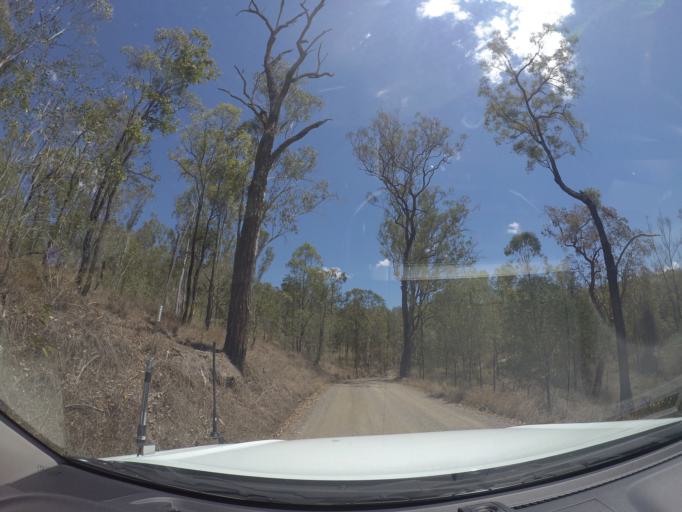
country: AU
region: Queensland
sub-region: Ipswich
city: Springfield Lakes
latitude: -27.8081
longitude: 152.8457
